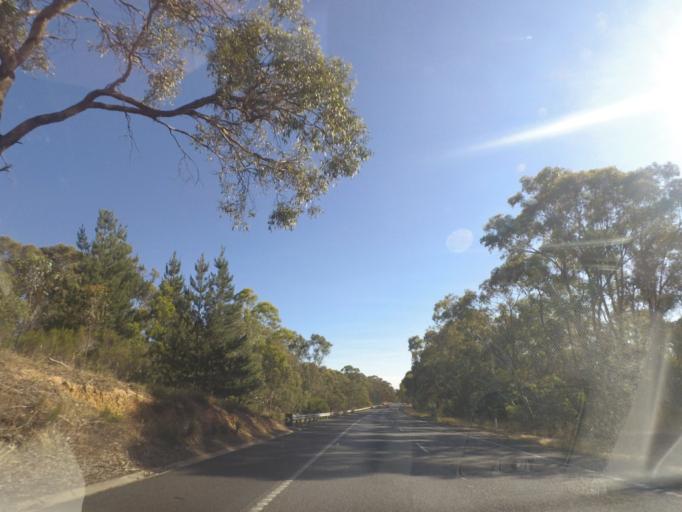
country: AU
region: Victoria
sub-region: Murrindindi
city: Kinglake West
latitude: -37.1723
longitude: 145.0753
